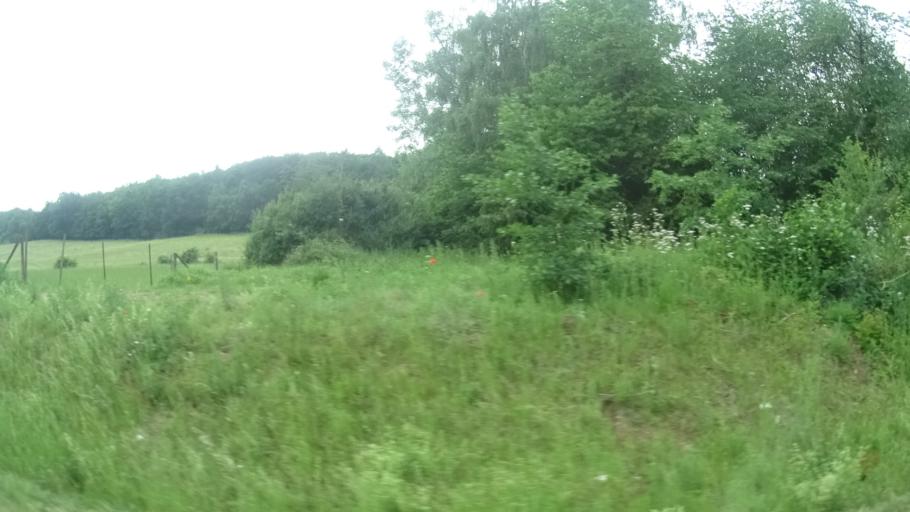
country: DE
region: Hesse
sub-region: Regierungsbezirk Kassel
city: Fulda
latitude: 50.5507
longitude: 9.6079
